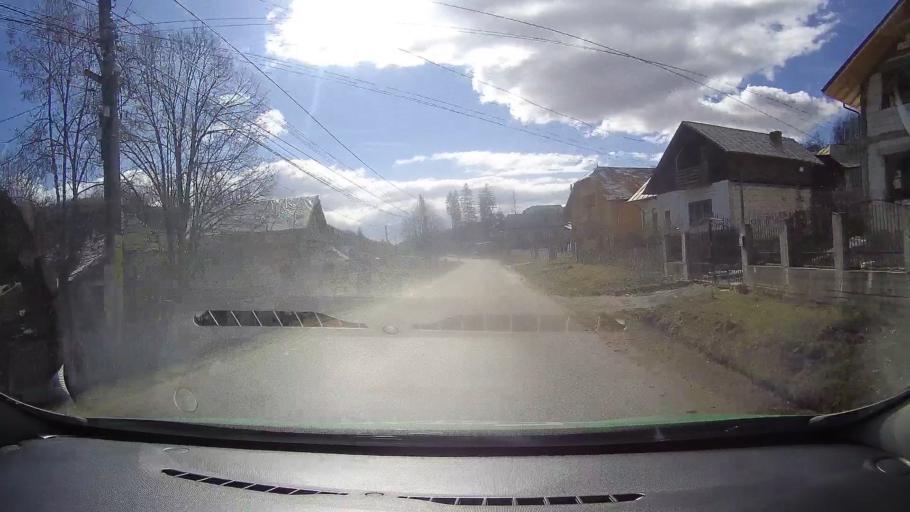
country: RO
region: Dambovita
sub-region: Comuna Vulcana Bai
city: Vulcana Bai
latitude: 45.0711
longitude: 25.3784
